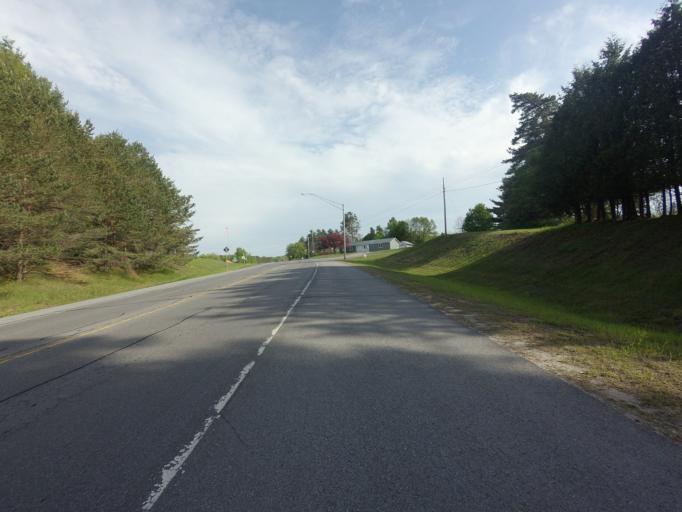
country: US
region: New York
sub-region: St. Lawrence County
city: Gouverneur
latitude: 44.1565
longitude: -75.3167
